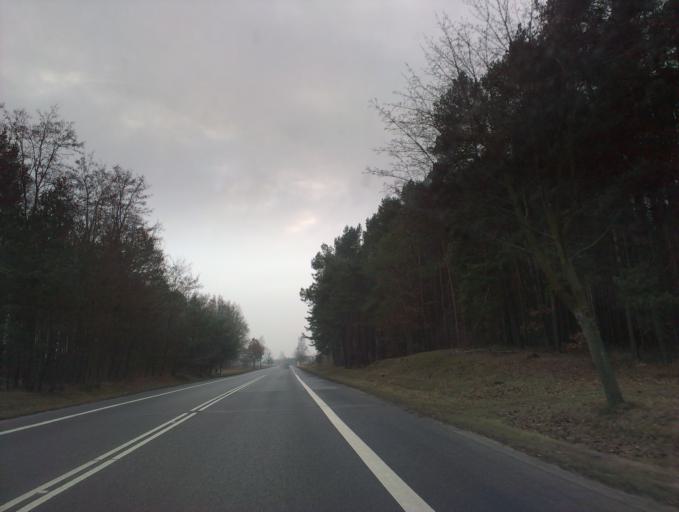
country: PL
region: Greater Poland Voivodeship
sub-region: Powiat chodzieski
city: Budzyn
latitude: 52.9078
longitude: 16.9726
